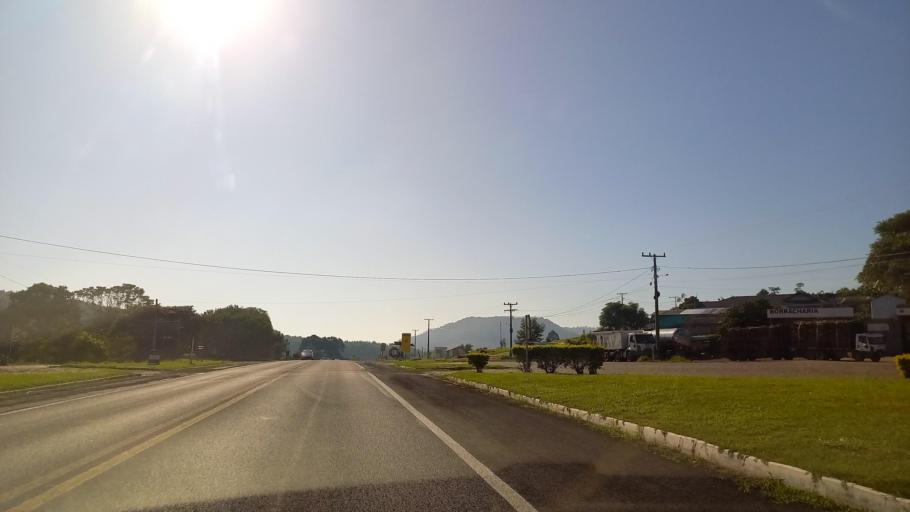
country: BR
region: Rio Grande do Sul
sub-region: Taquari
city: Taquari
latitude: -29.7096
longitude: -51.7658
